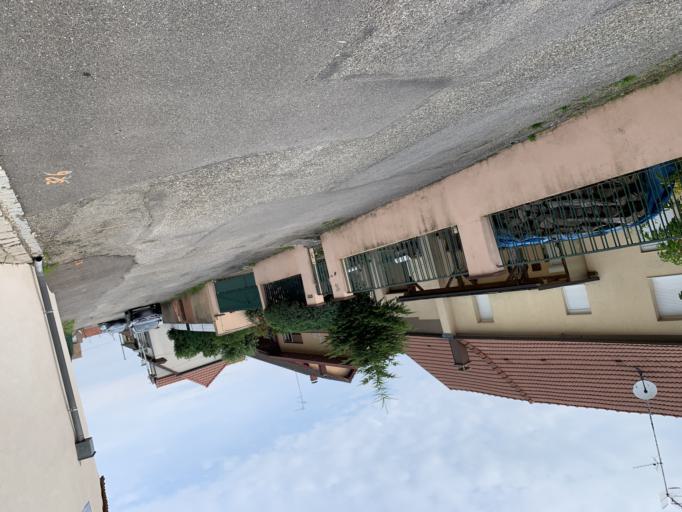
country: FR
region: Alsace
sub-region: Departement du Haut-Rhin
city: Morschwiller-le-Bas
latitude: 47.7351
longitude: 7.2649
